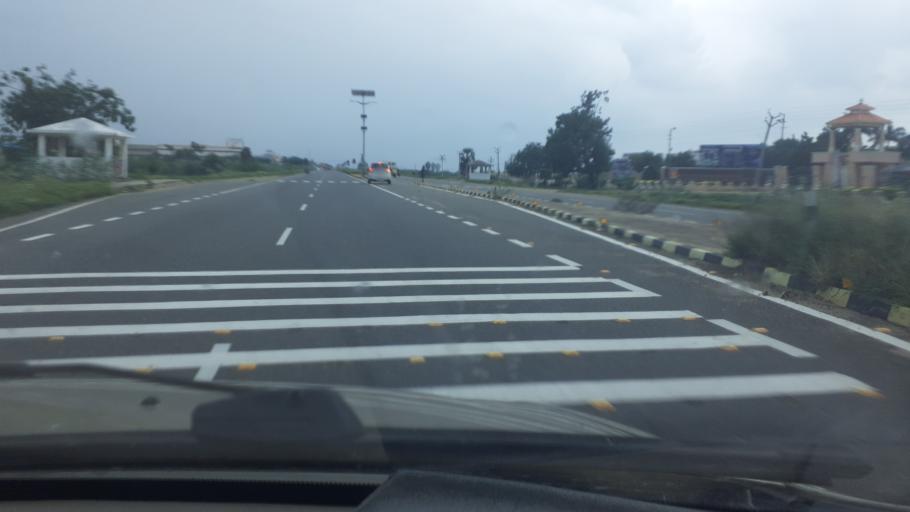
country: IN
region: Tamil Nadu
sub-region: Virudhunagar
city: Virudunagar
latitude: 9.6736
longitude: 77.9670
